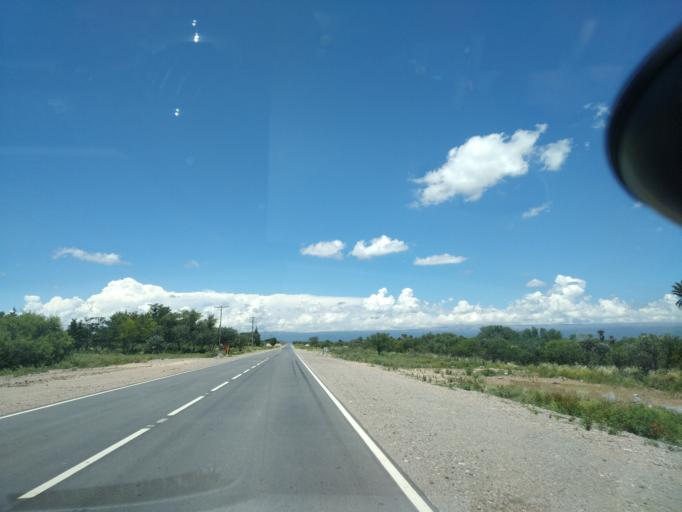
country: AR
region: Cordoba
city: Salsacate
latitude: -31.3667
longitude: -65.2259
